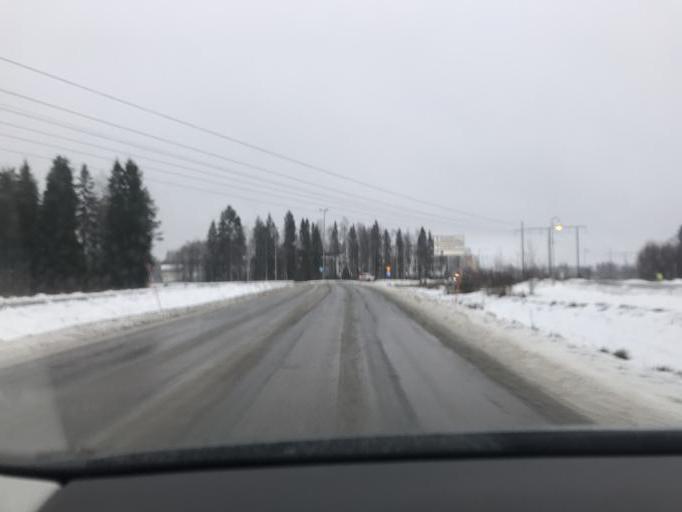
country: SE
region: Norrbotten
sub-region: Lulea Kommun
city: Bergnaset
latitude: 65.6145
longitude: 22.1212
